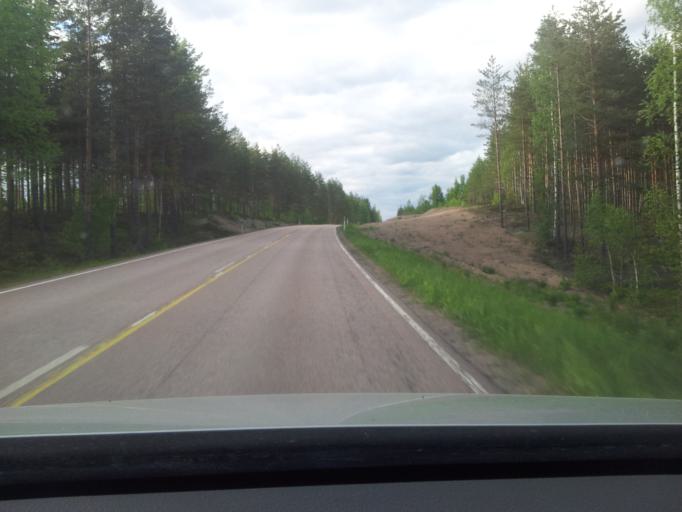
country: FI
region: South Karelia
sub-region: Lappeenranta
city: Luumaeki
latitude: 60.9366
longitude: 27.5830
